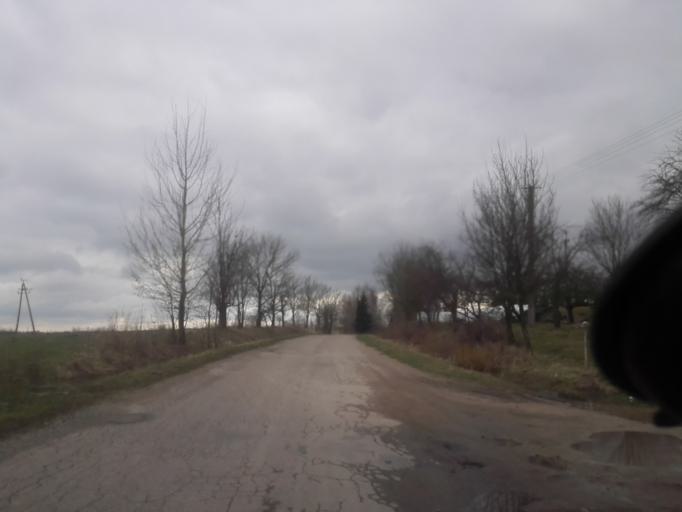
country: PL
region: Podlasie
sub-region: Suwalki
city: Suwalki
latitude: 54.2463
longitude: 22.9925
